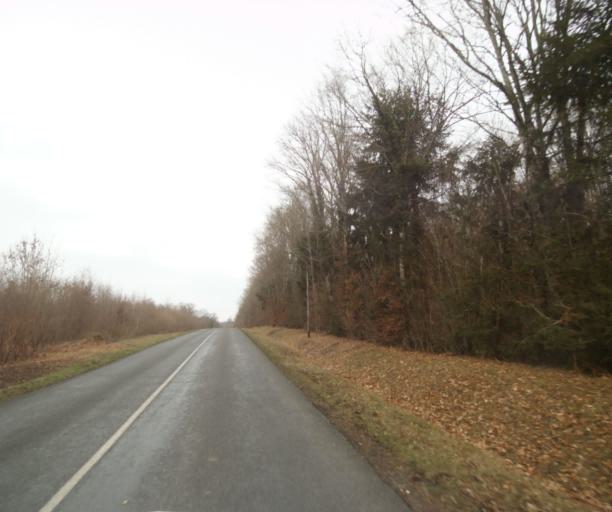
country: FR
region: Champagne-Ardenne
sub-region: Departement de la Haute-Marne
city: Villiers-en-Lieu
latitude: 48.7004
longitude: 4.8953
